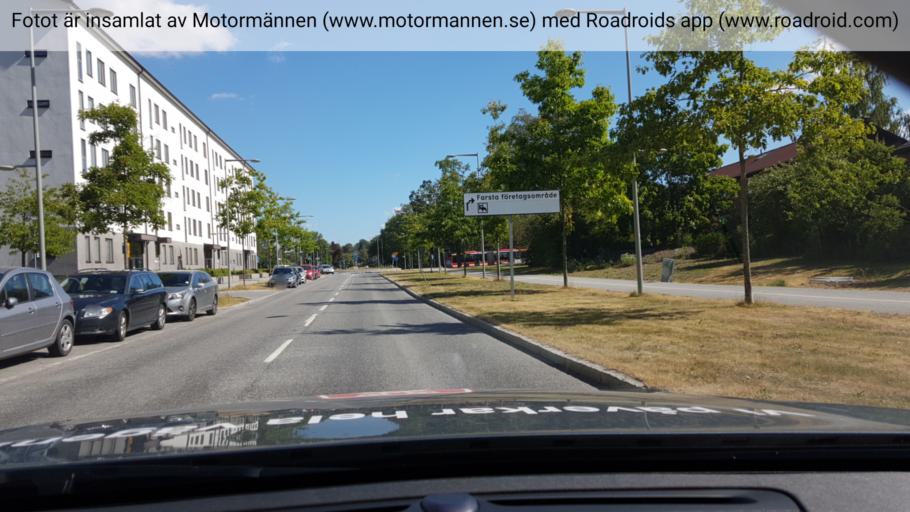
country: SE
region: Stockholm
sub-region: Stockholms Kommun
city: Arsta
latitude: 59.2407
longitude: 18.1030
